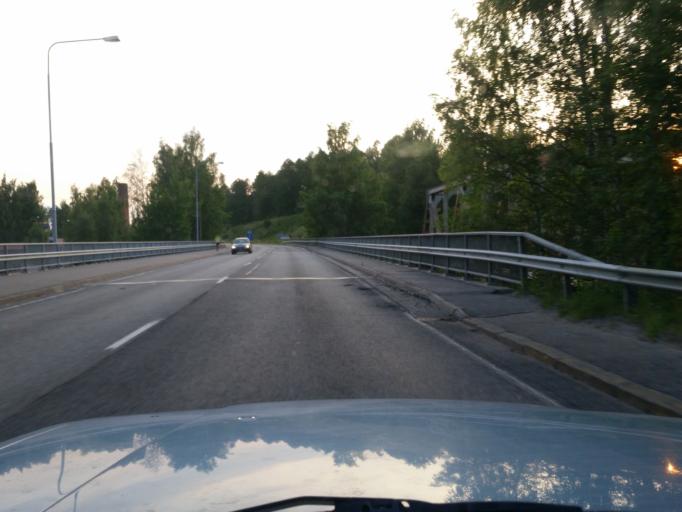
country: FI
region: Southern Savonia
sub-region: Savonlinna
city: Savonlinna
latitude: 61.8785
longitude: 28.8391
